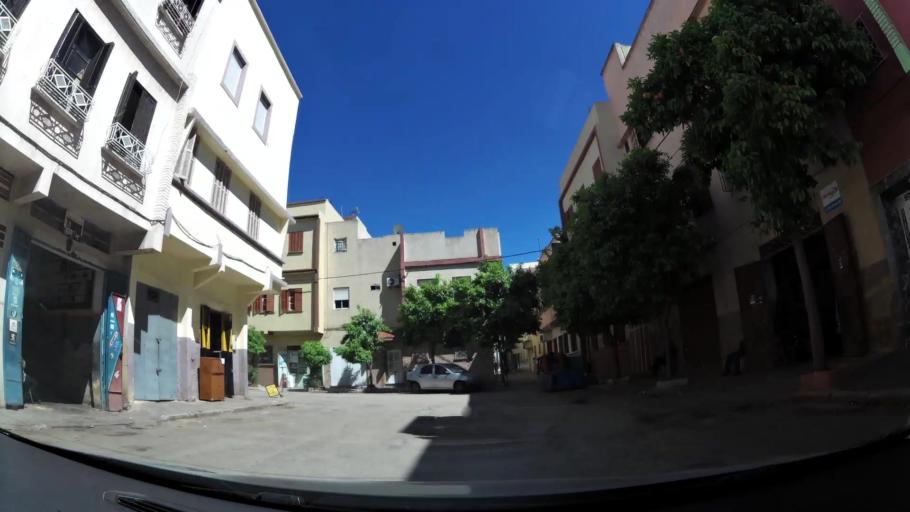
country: MA
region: Meknes-Tafilalet
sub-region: Meknes
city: Meknes
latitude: 33.8854
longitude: -5.5706
